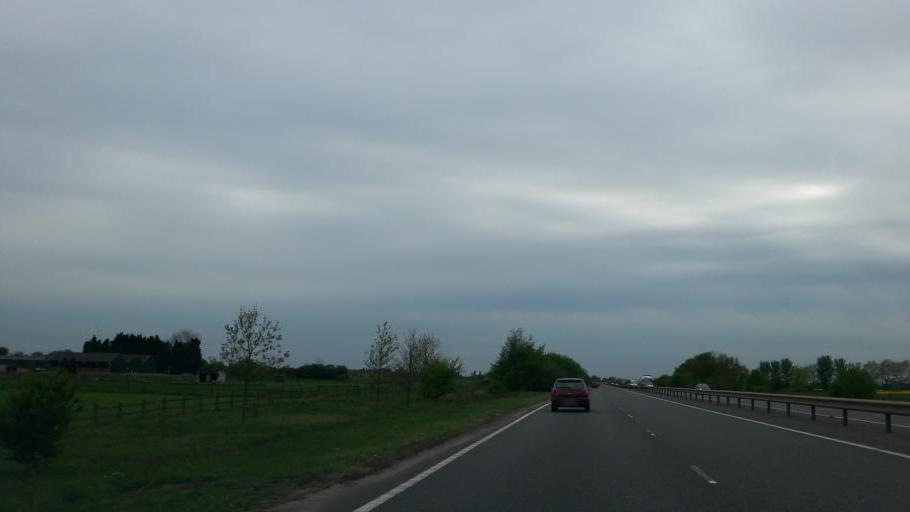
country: GB
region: England
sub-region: Peterborough
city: Thorney
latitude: 52.6221
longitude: -0.0690
